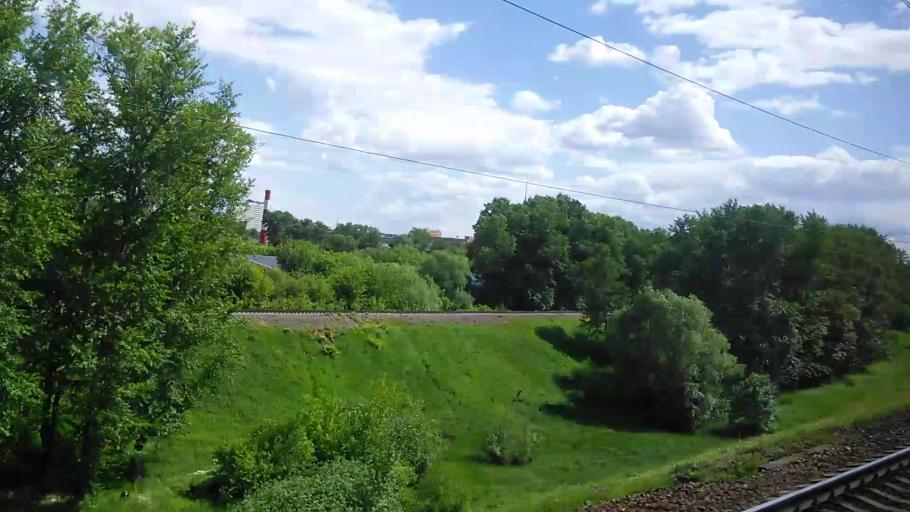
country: RU
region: Moscow
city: Likhobory
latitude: 55.8554
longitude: 37.5730
